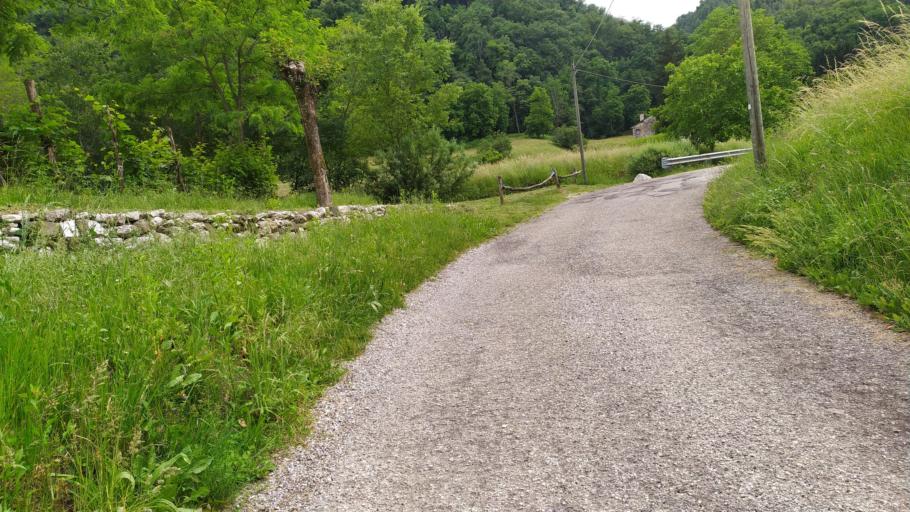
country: IT
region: Veneto
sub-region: Provincia di Vicenza
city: Schio
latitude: 45.6939
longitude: 11.3365
